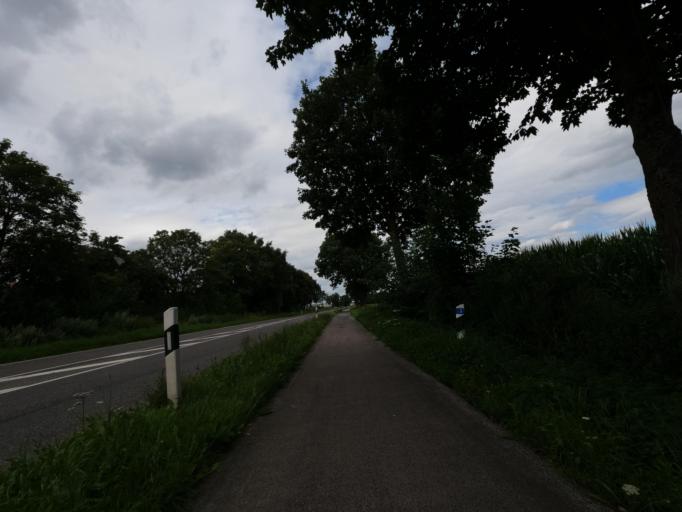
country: DE
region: North Rhine-Westphalia
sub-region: Regierungsbezirk Koln
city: Ubach-Palenberg
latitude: 50.9214
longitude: 6.1369
